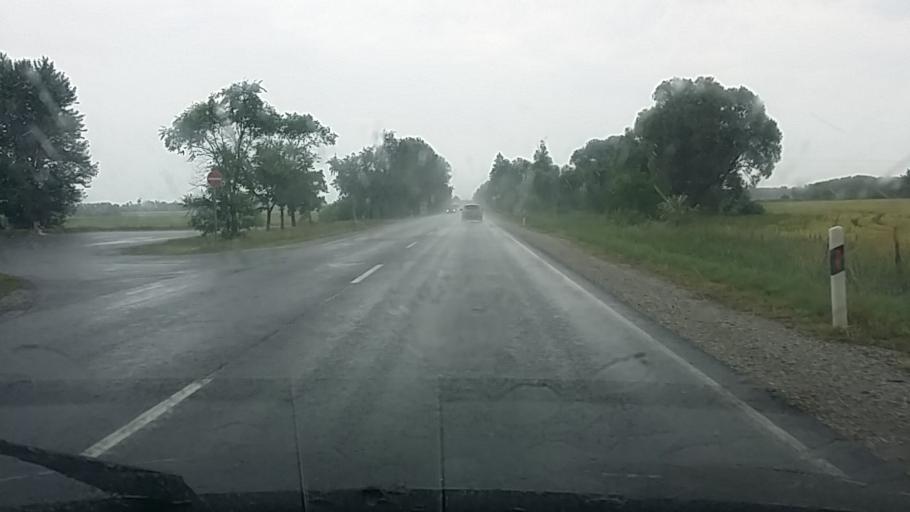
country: HU
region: Szabolcs-Szatmar-Bereg
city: Ujfeherto
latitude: 47.8700
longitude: 21.7053
